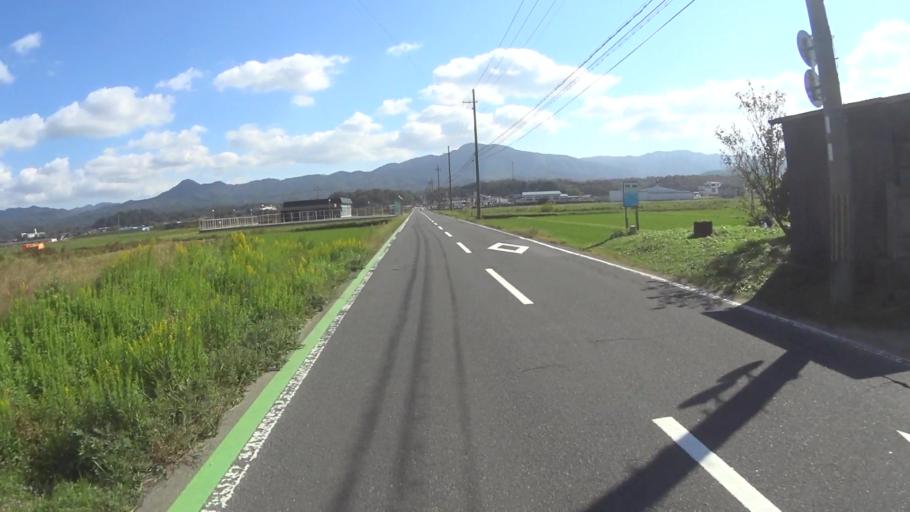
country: JP
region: Kyoto
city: Miyazu
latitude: 35.6705
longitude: 135.0822
